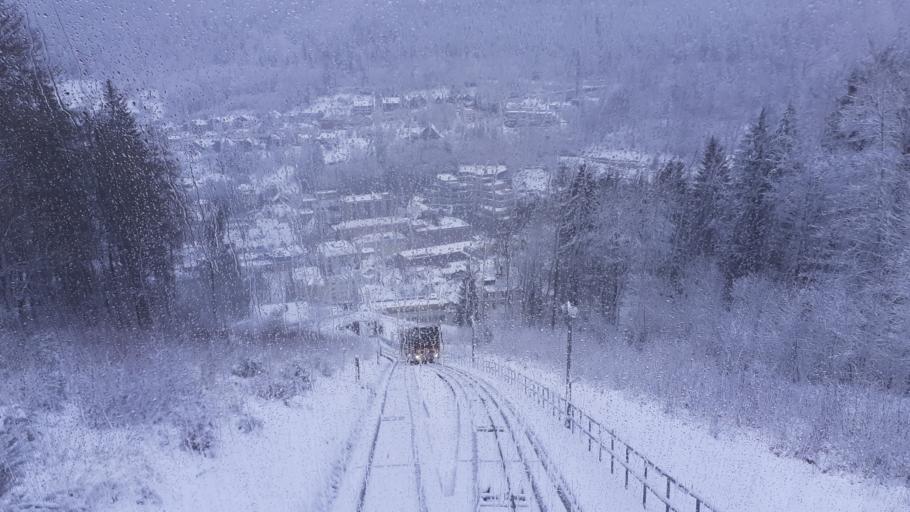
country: DE
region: Baden-Wuerttemberg
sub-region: Karlsruhe Region
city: Bad Wildbad
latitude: 48.7502
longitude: 8.5438
